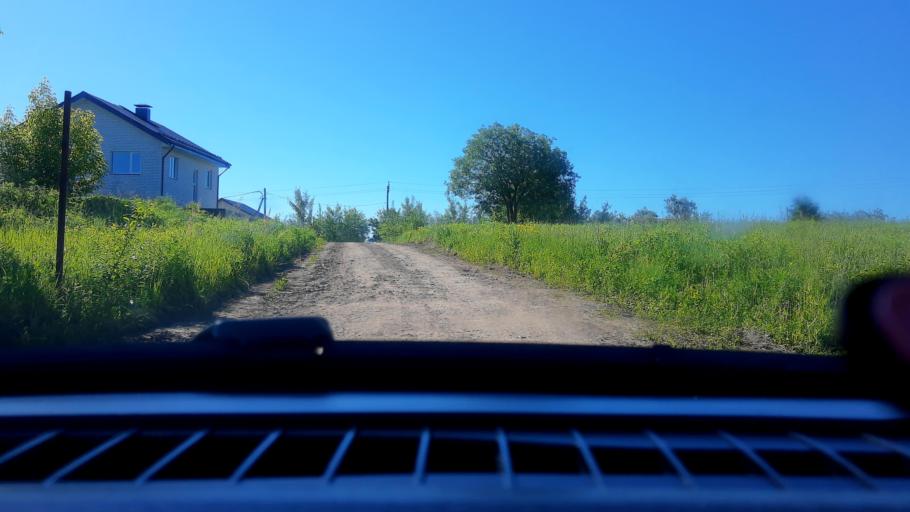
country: RU
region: Nizjnij Novgorod
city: Afonino
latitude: 56.2563
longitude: 44.0525
